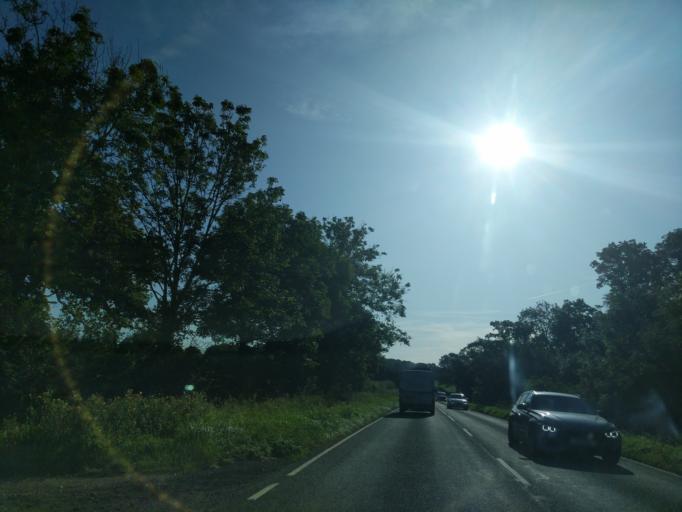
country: GB
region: England
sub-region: District of Rutland
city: Clipsham
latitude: 52.8031
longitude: -0.5821
